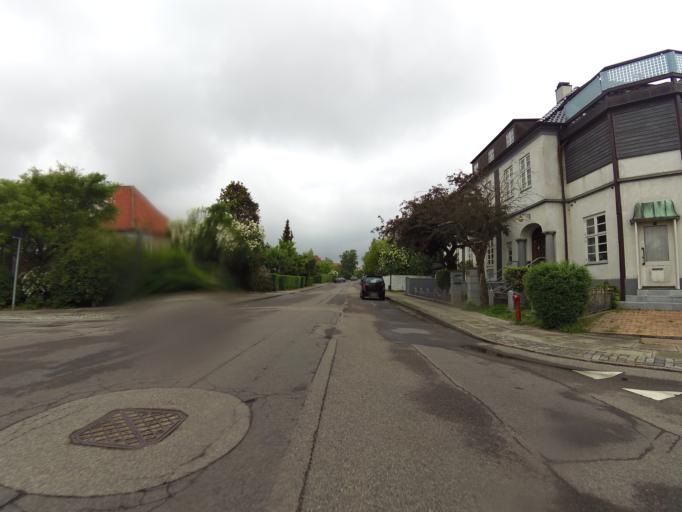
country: DK
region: Capital Region
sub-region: Frederiksberg Kommune
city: Frederiksberg
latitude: 55.7253
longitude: 12.5421
